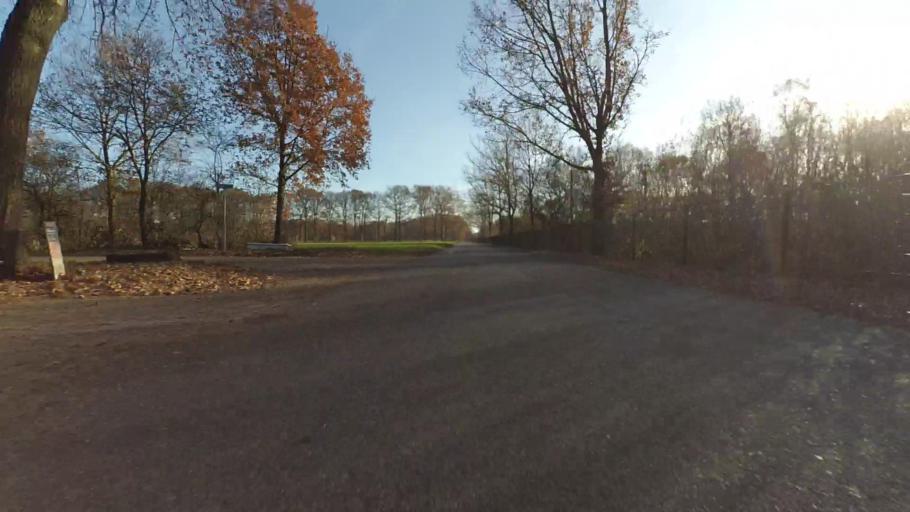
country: NL
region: Utrecht
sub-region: Gemeente Utrechtse Heuvelrug
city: Overberg
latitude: 52.0354
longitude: 5.5085
